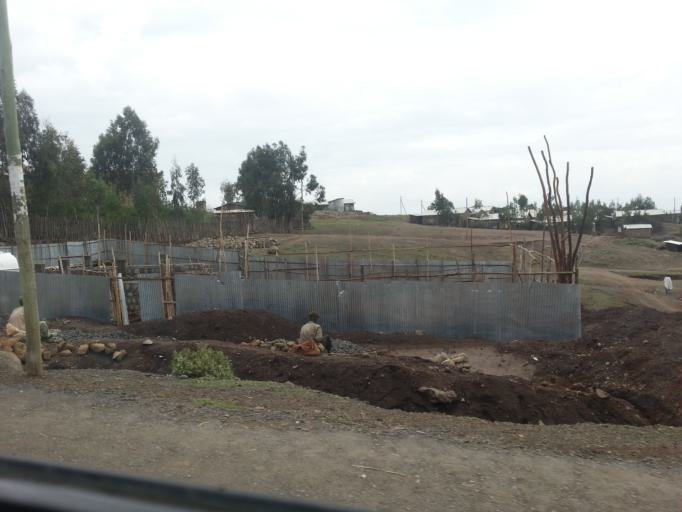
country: ET
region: Amhara
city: Lalibela
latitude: 12.0268
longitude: 39.0495
